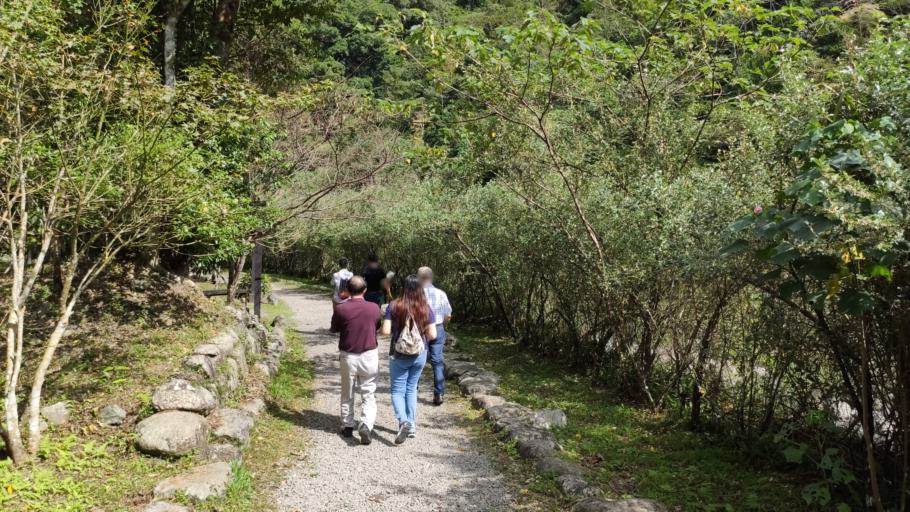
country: TW
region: Taiwan
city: Daxi
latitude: 24.8313
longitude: 121.4460
